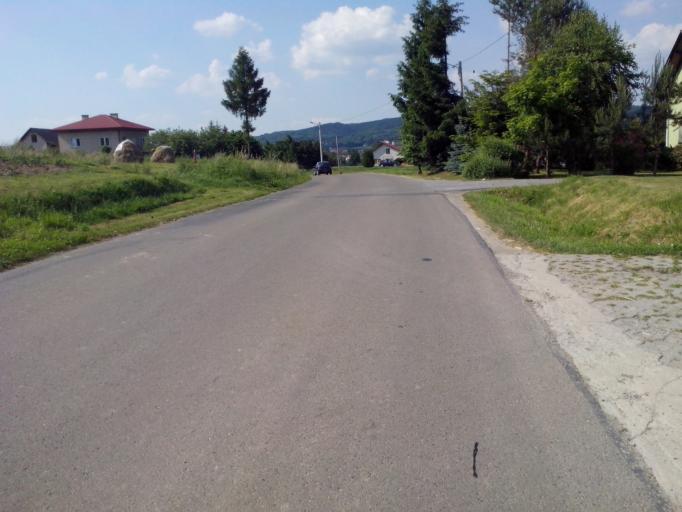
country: PL
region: Subcarpathian Voivodeship
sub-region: Powiat brzozowski
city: Blizne
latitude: 49.7449
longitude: 21.9739
